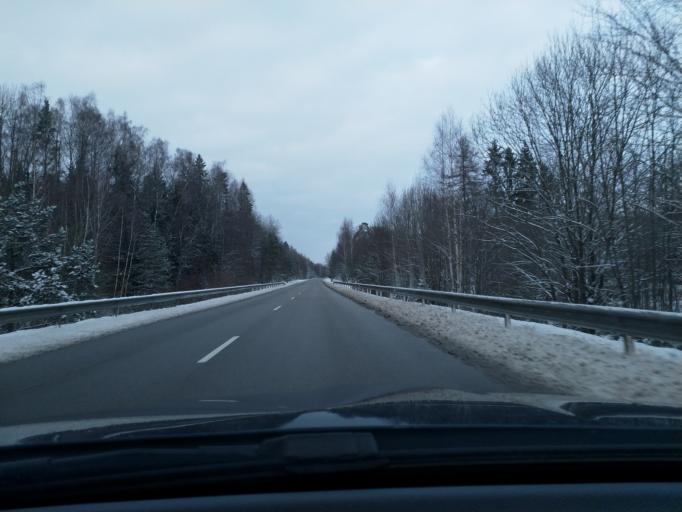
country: LV
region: Kuldigas Rajons
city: Kuldiga
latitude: 56.9457
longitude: 21.9350
